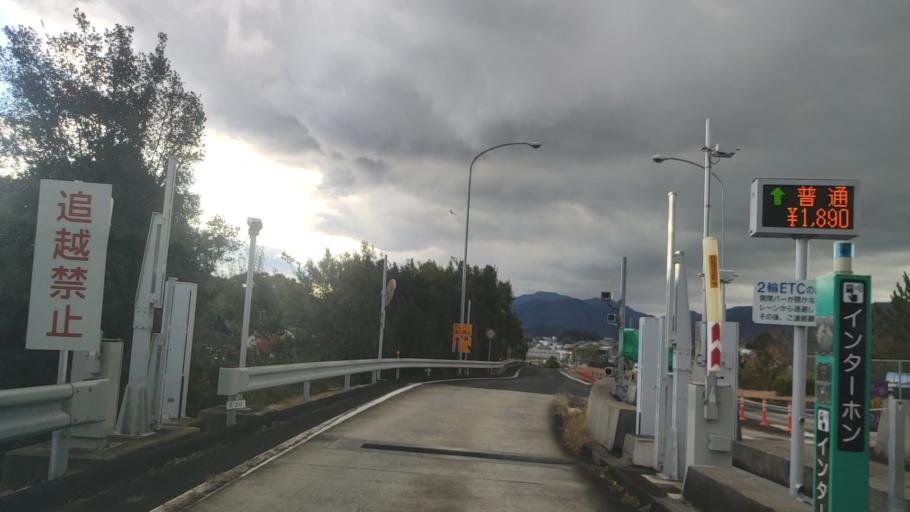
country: JP
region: Hyogo
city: Sumoto
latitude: 34.3425
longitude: 134.8478
